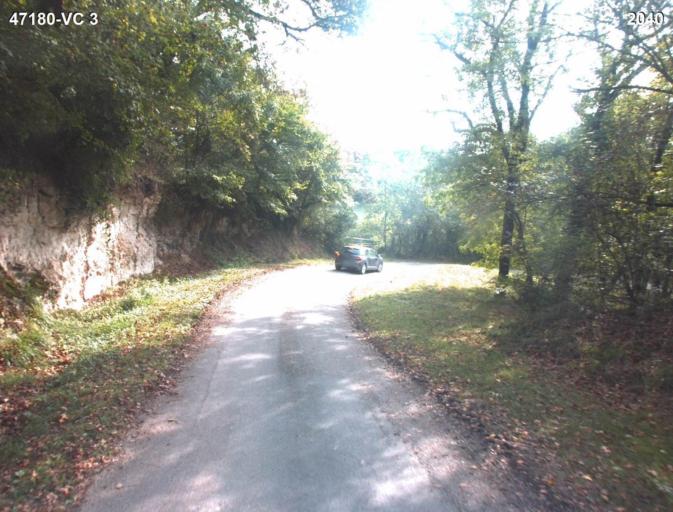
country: FR
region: Aquitaine
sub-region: Departement du Lot-et-Garonne
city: Sainte-Colombe-en-Bruilhois
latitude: 44.1524
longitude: 0.4416
